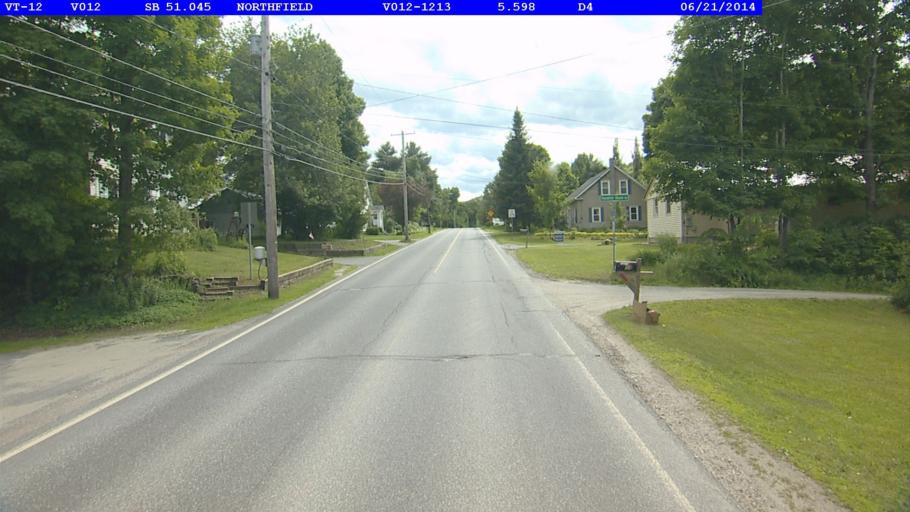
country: US
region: Vermont
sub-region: Washington County
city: Northfield
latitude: 44.1684
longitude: -72.6532
